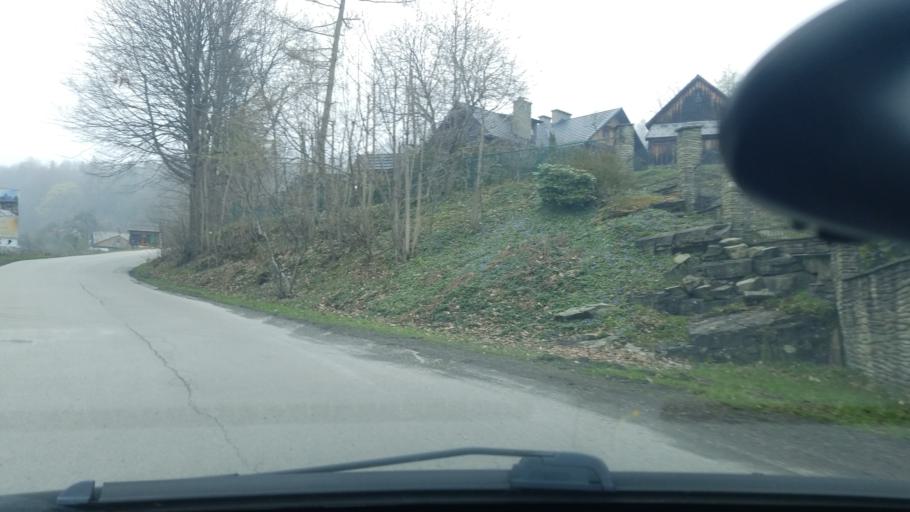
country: PL
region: Silesian Voivodeship
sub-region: Powiat cieszynski
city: Ustron
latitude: 49.7138
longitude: 18.8516
